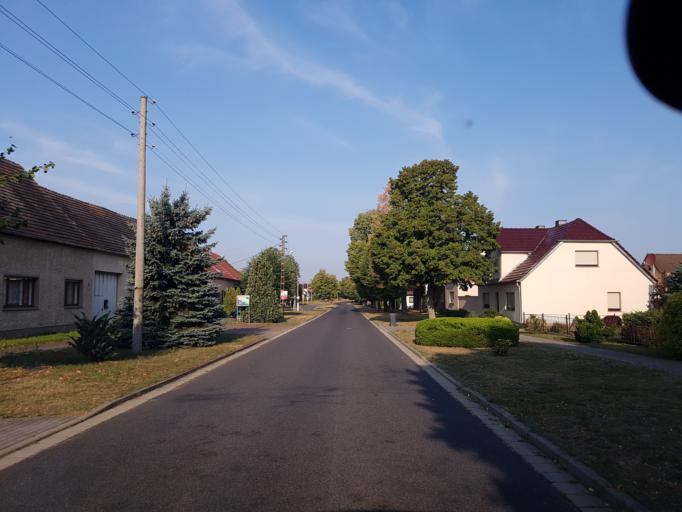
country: DE
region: Brandenburg
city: Finsterwalde
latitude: 51.6657
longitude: 13.7363
